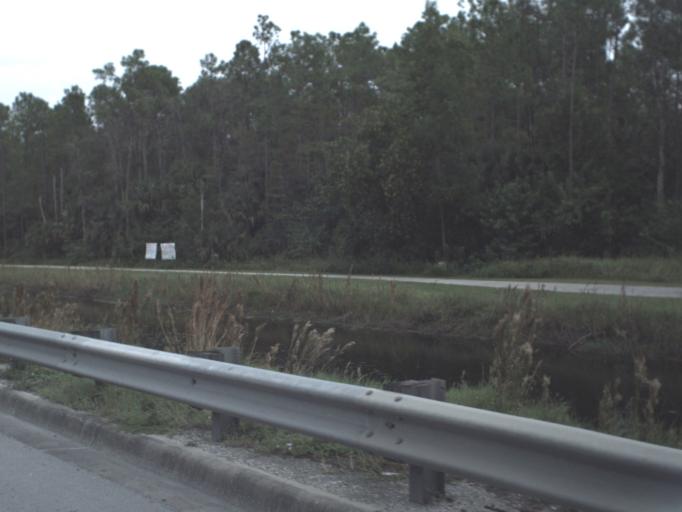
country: US
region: Florida
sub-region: Collier County
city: Lely
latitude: 26.1330
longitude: -81.6868
